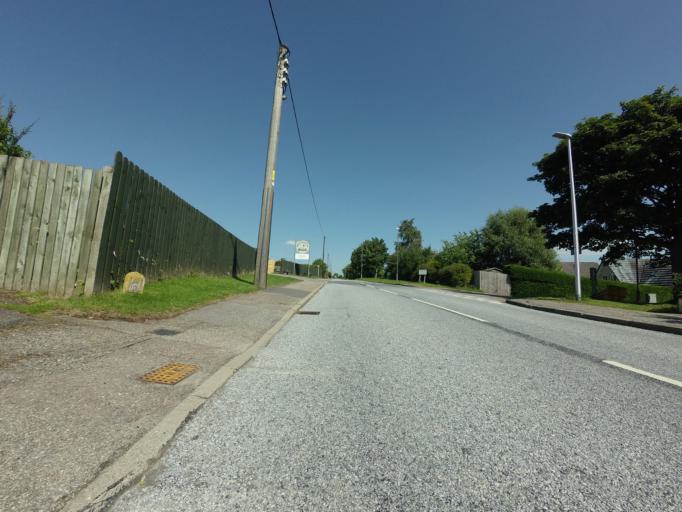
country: GB
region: Scotland
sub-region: Highland
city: Dingwall
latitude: 57.6057
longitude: -4.4269
